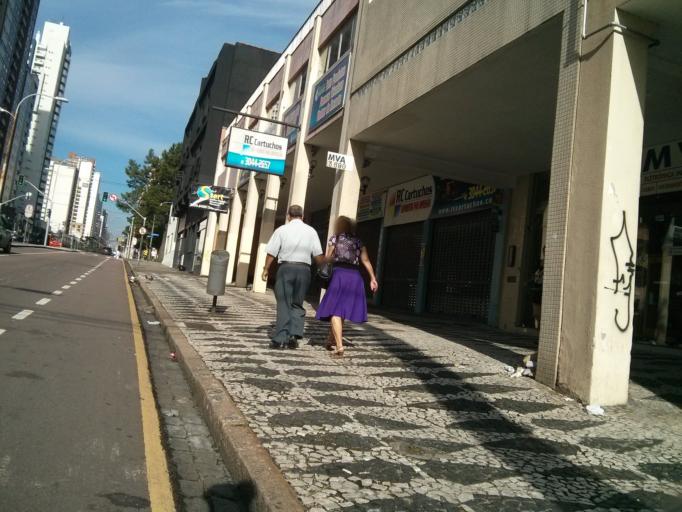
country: BR
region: Parana
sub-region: Curitiba
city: Curitiba
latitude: -25.4405
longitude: -49.2745
